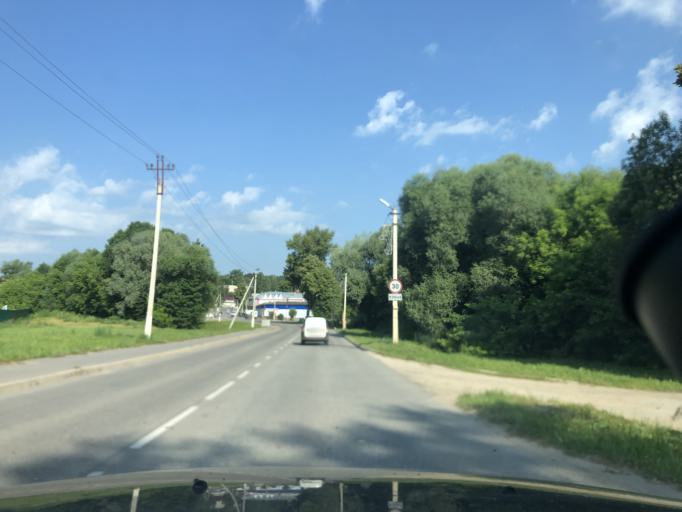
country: RU
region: Tula
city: Dubna
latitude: 54.1499
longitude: 36.9684
